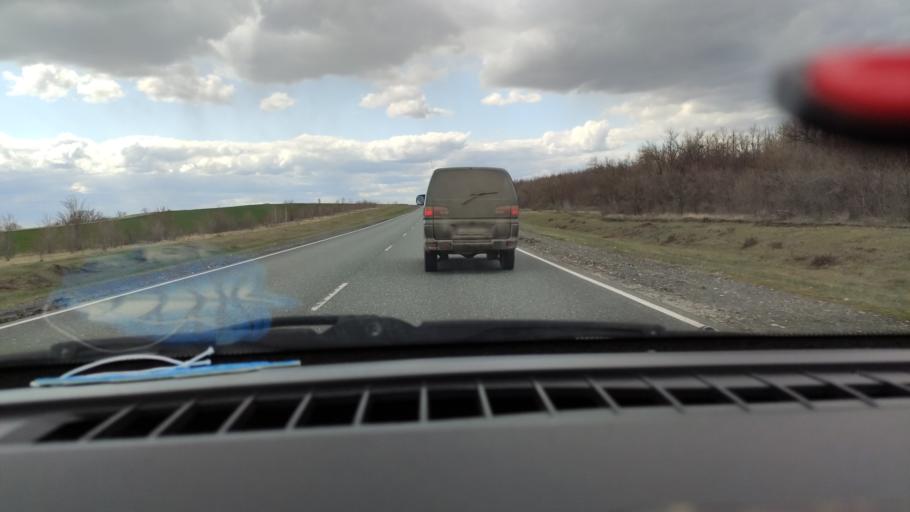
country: RU
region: Saratov
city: Balakovo
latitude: 52.1921
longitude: 47.8546
